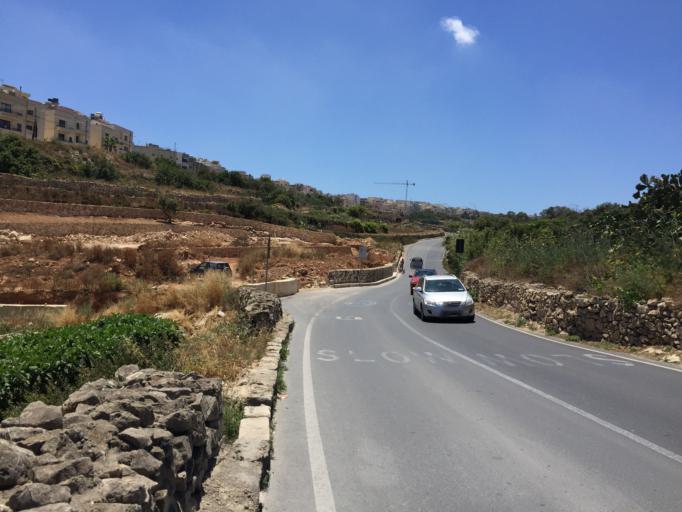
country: MT
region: Is-Swieqi
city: Swieqi
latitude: 35.9169
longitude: 14.4802
